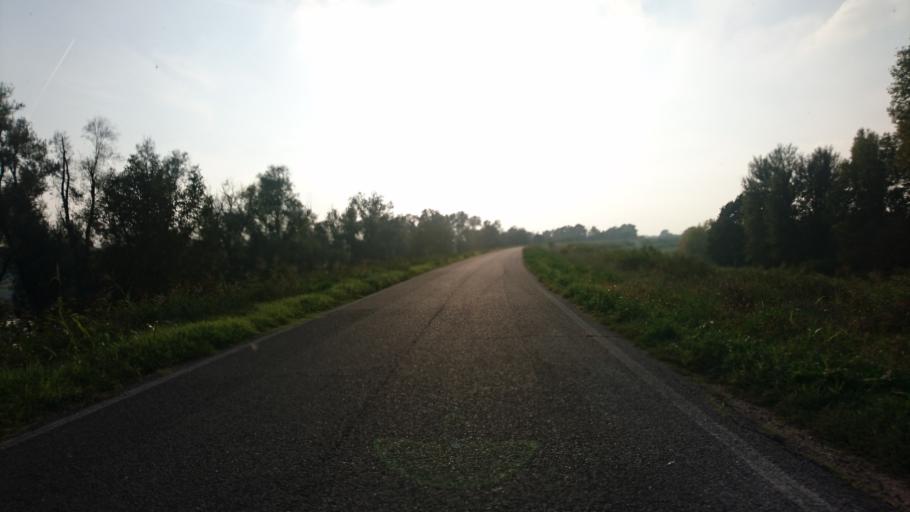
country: IT
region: Veneto
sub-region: Provincia di Rovigo
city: Canaro
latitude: 44.9200
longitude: 11.6907
